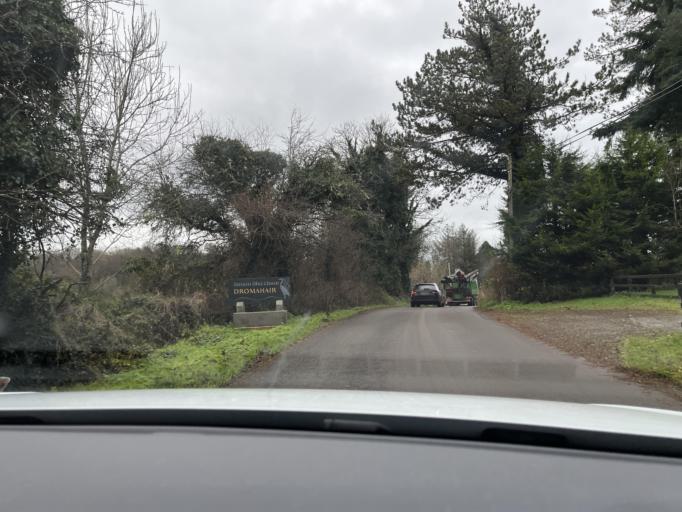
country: IE
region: Connaught
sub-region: County Leitrim
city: Manorhamilton
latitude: 54.2302
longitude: -8.2852
